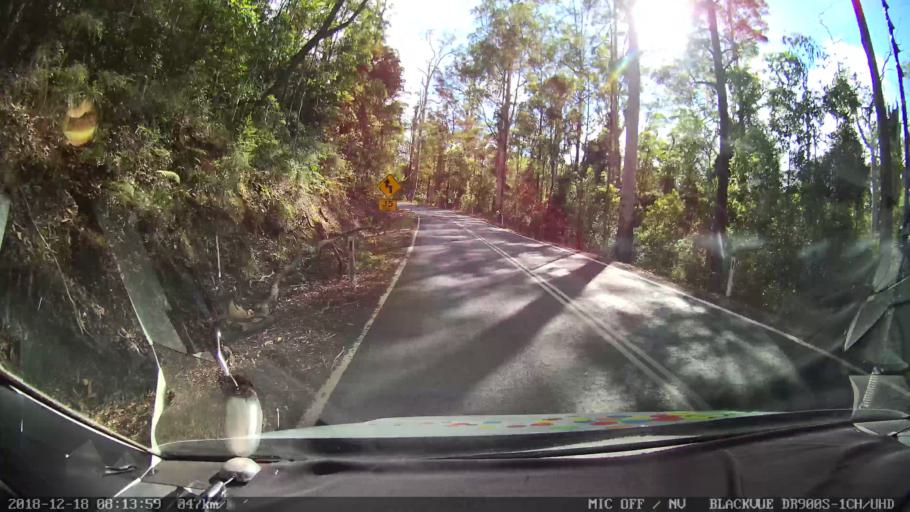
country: AU
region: New South Wales
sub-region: Kyogle
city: Kyogle
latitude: -28.3374
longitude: 152.6795
